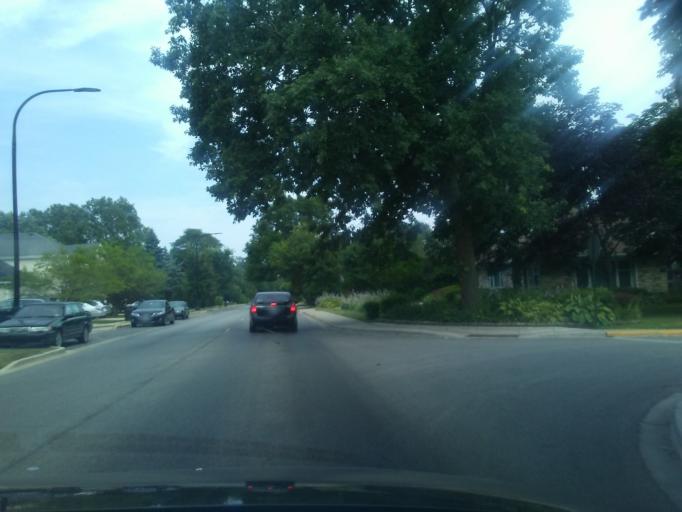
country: US
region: Illinois
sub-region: Cook County
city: Lincolnwood
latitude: 42.0046
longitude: -87.7606
